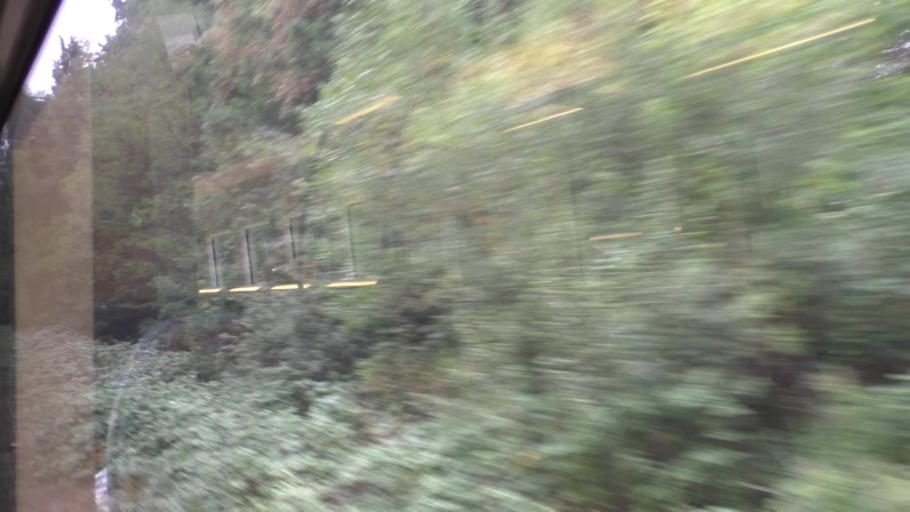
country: DE
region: Saxony
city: Goerlitz
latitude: 51.1638
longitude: 14.9616
